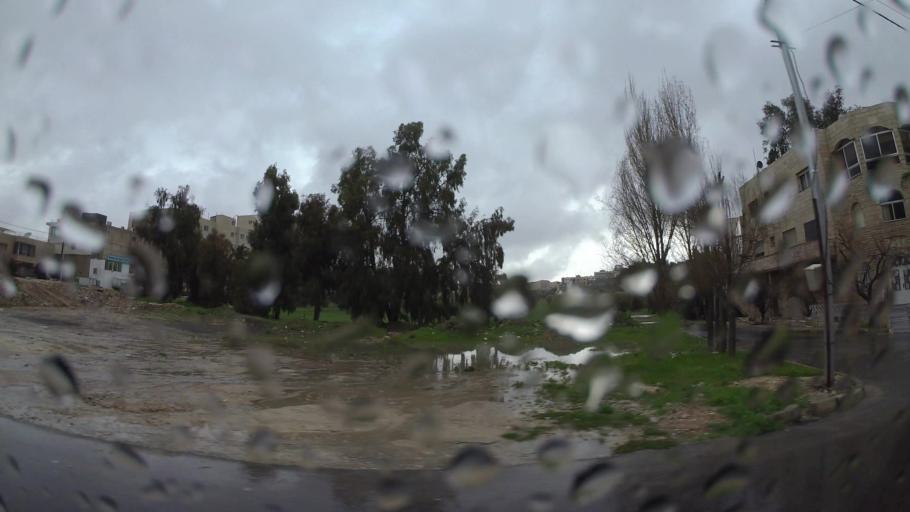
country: JO
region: Amman
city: Al Jubayhah
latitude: 32.0260
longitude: 35.8582
